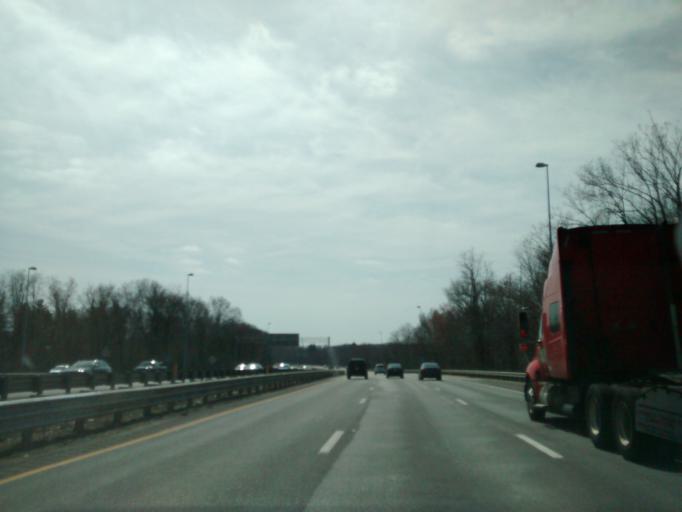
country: US
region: Massachusetts
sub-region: Worcester County
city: Worcester
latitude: 42.2324
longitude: -71.8235
